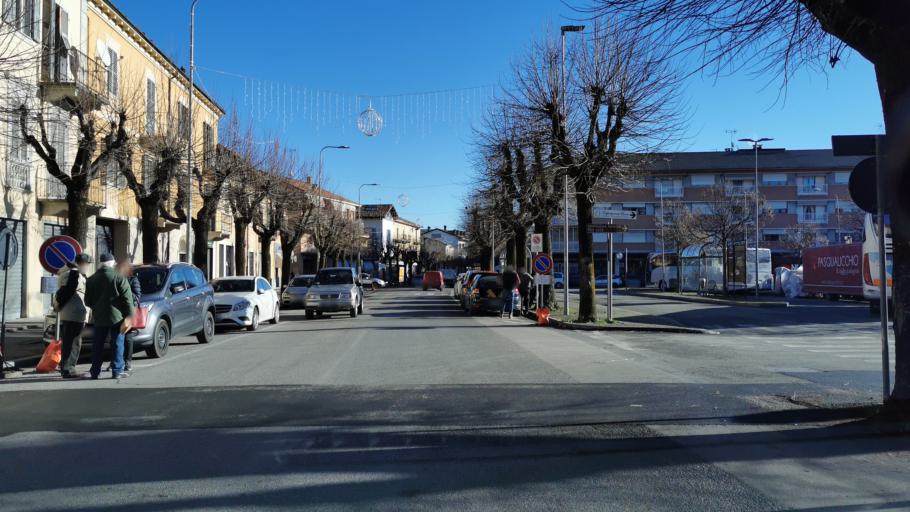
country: IT
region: Piedmont
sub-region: Provincia di Cuneo
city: Carru
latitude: 44.4794
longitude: 7.8740
